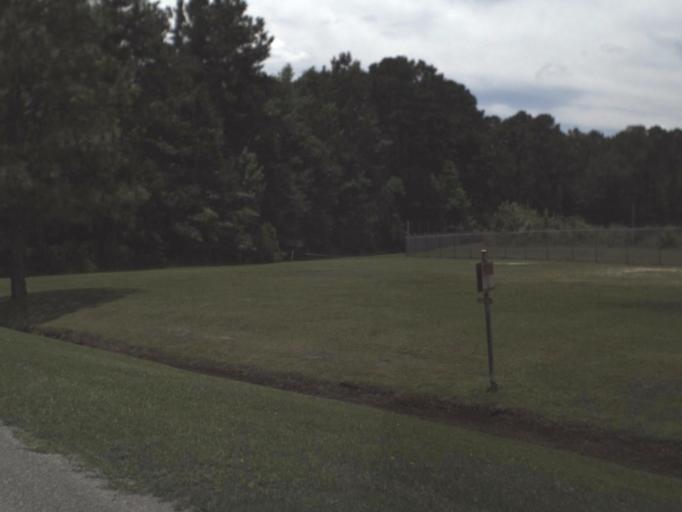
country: US
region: Florida
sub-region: Nassau County
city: Nassau Village-Ratliff
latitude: 30.4447
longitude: -81.7670
